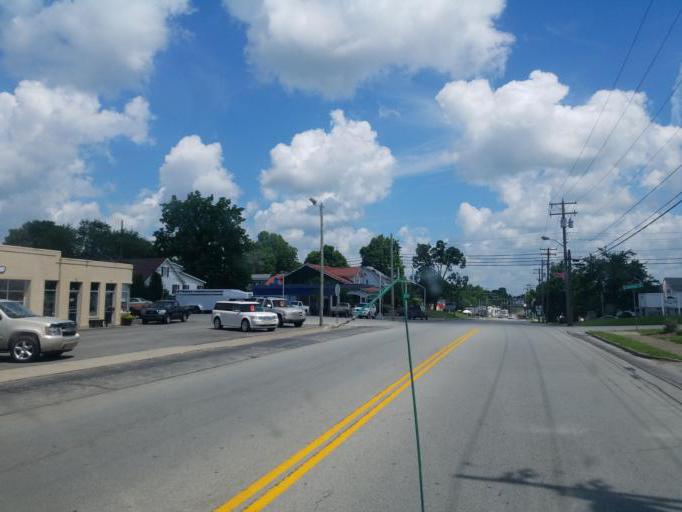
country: US
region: Kentucky
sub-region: Grayson County
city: Leitchfield
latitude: 37.4824
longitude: -86.2934
